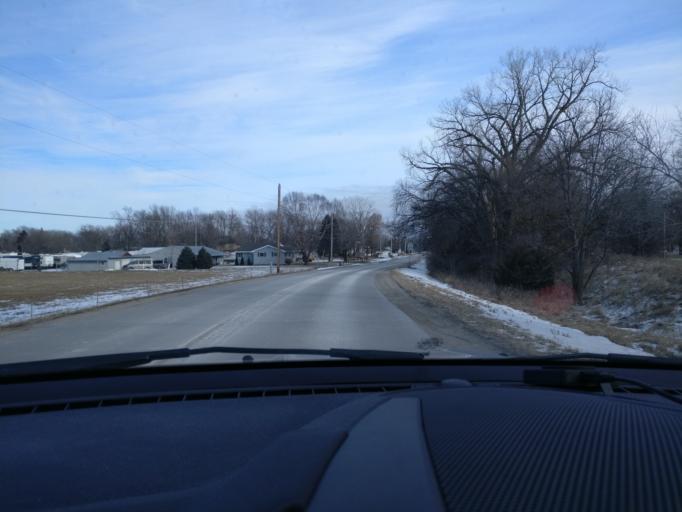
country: US
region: Nebraska
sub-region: Dodge County
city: Fremont
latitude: 41.4142
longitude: -96.5078
